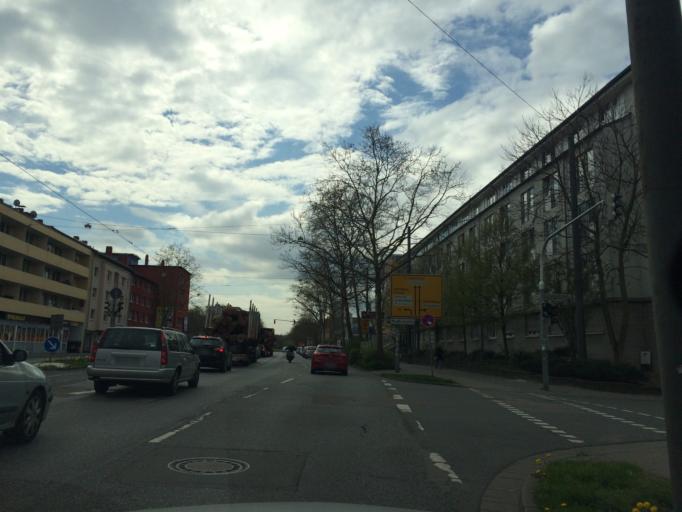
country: DE
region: Hesse
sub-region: Regierungsbezirk Darmstadt
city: Darmstadt
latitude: 49.8697
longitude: 8.6453
